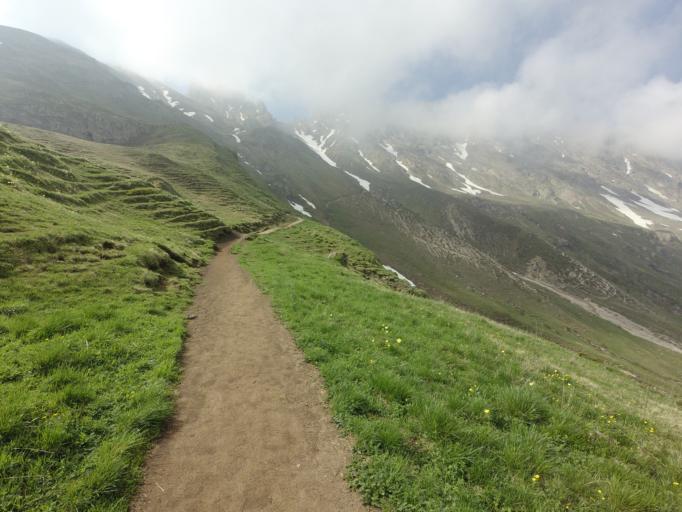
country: IT
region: Trentino-Alto Adige
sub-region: Bolzano
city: Ortisei
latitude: 46.5082
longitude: 11.6350
